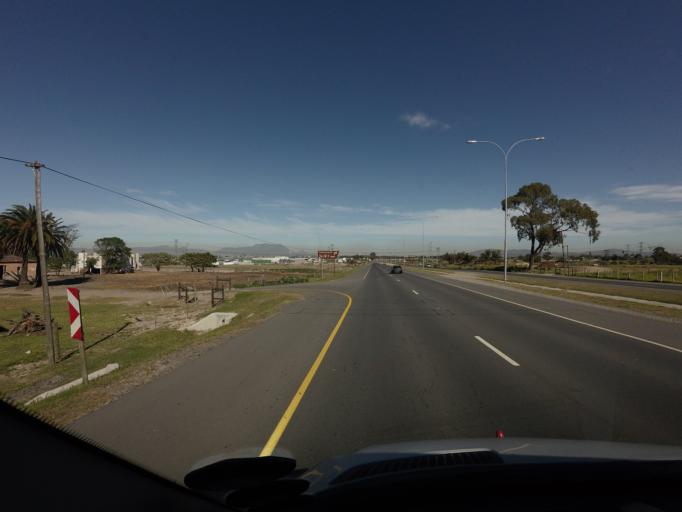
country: ZA
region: Western Cape
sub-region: City of Cape Town
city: Kraaifontein
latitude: -33.9511
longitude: 18.7102
